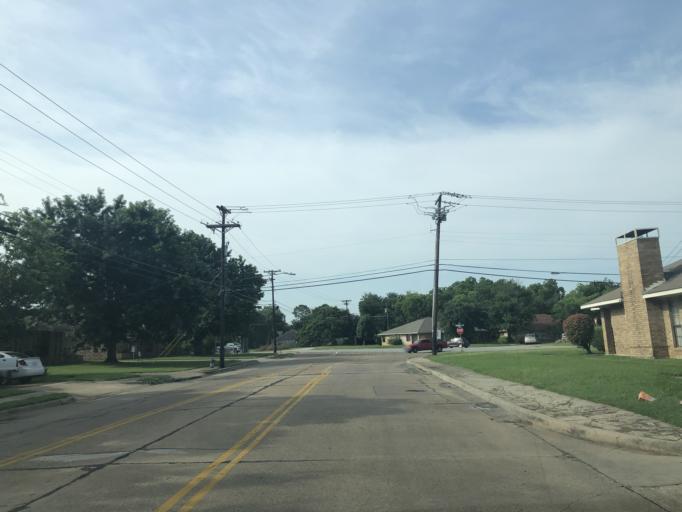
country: US
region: Texas
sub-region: Dallas County
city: Irving
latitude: 32.8023
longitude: -96.9630
